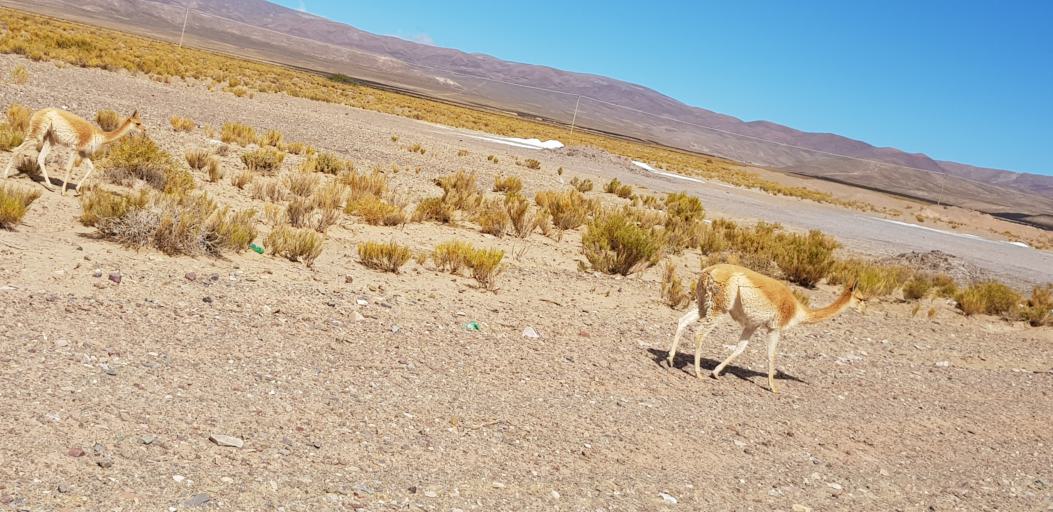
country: AR
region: Jujuy
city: Maimara
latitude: -23.6436
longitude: -65.8400
